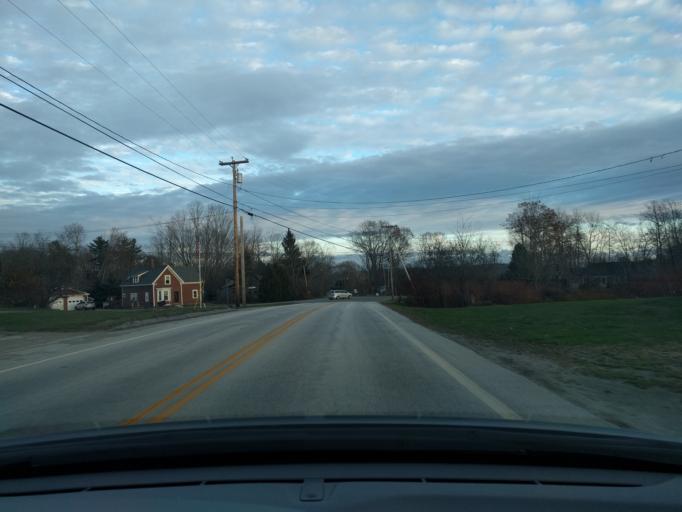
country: US
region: Maine
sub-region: Waldo County
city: Winterport
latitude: 44.6420
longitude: -68.8552
